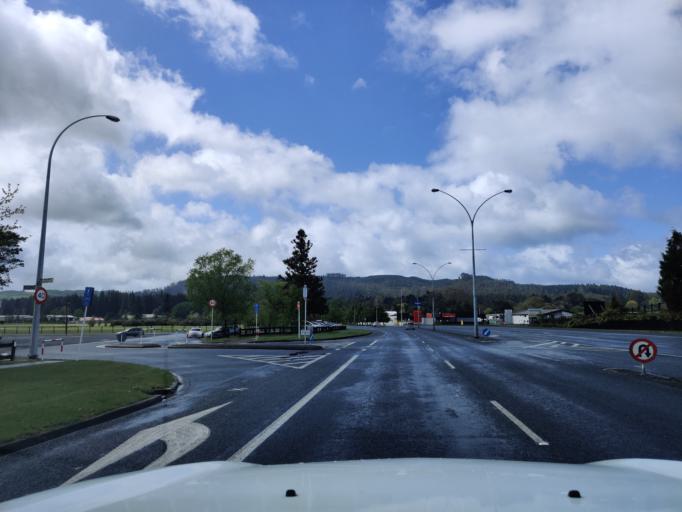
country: NZ
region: Bay of Plenty
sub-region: Rotorua District
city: Rotorua
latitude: -38.1471
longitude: 176.2604
